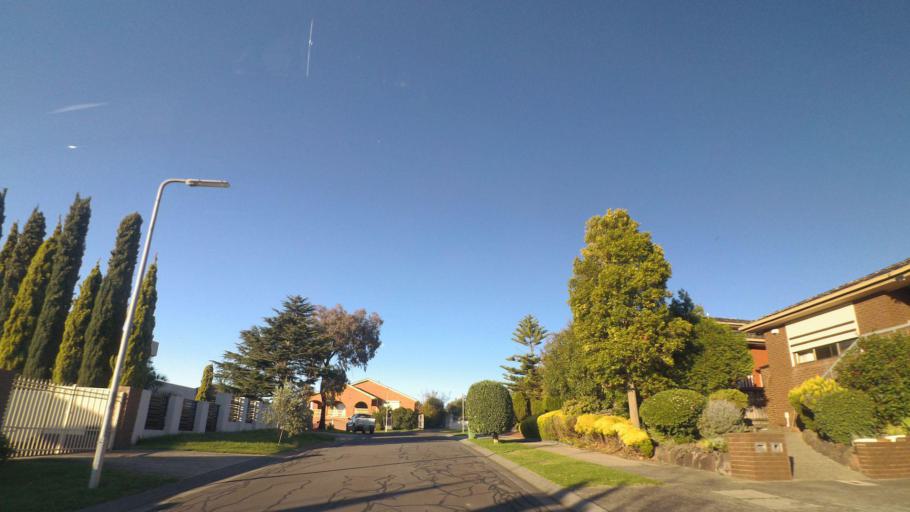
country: AU
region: Victoria
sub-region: Banyule
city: Greensborough
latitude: -37.6865
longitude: 145.1078
